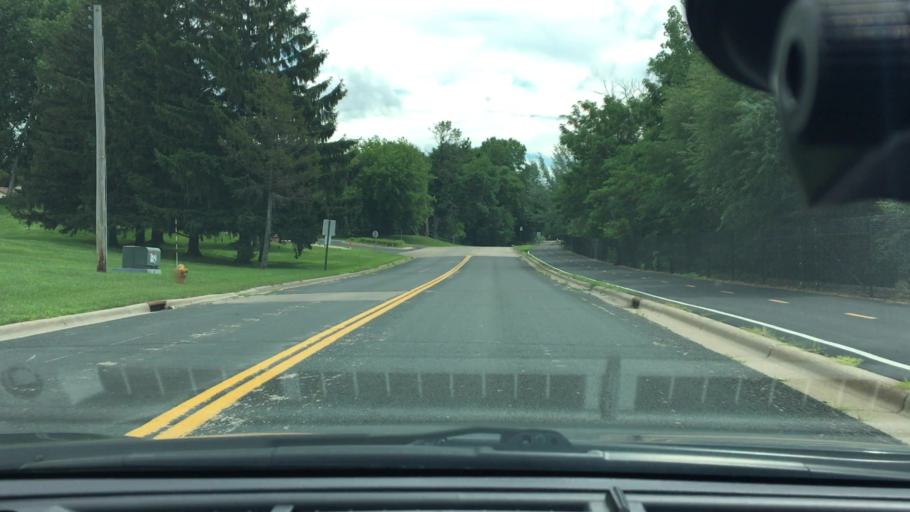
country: US
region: Minnesota
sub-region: Hennepin County
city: Plymouth
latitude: 45.0155
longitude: -93.4181
